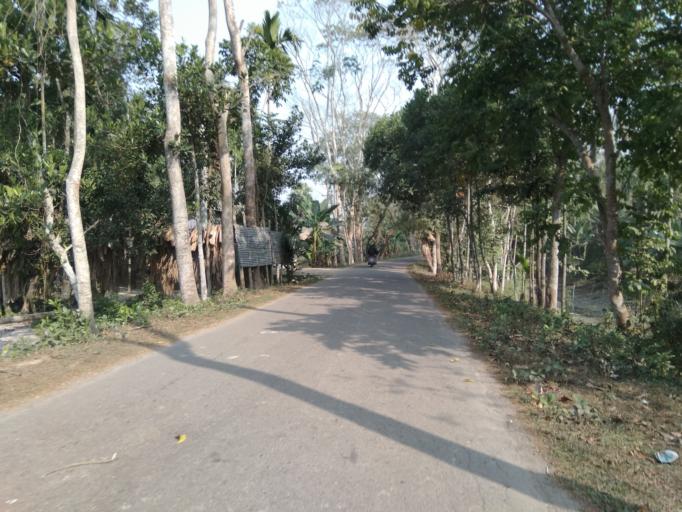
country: BD
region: Barisal
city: Mehendiganj
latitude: 22.9619
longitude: 90.4146
